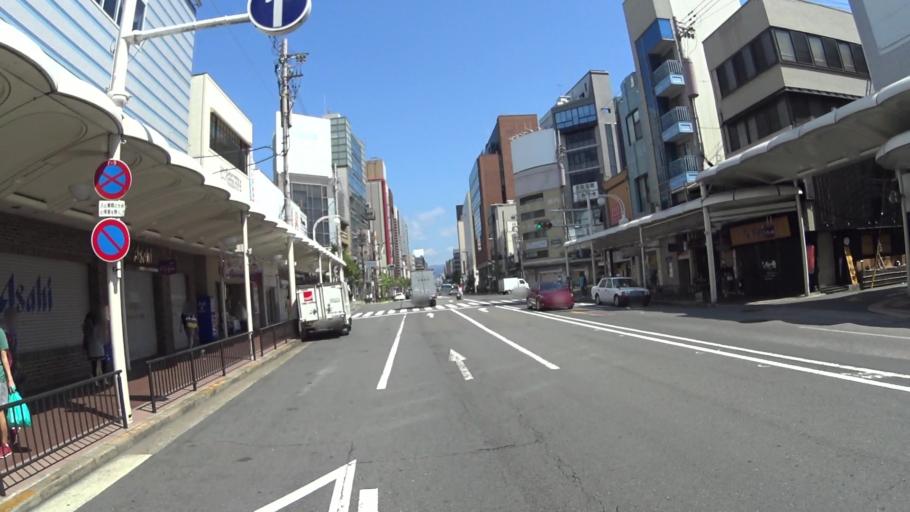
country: JP
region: Kyoto
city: Kyoto
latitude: 35.0073
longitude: 135.7694
